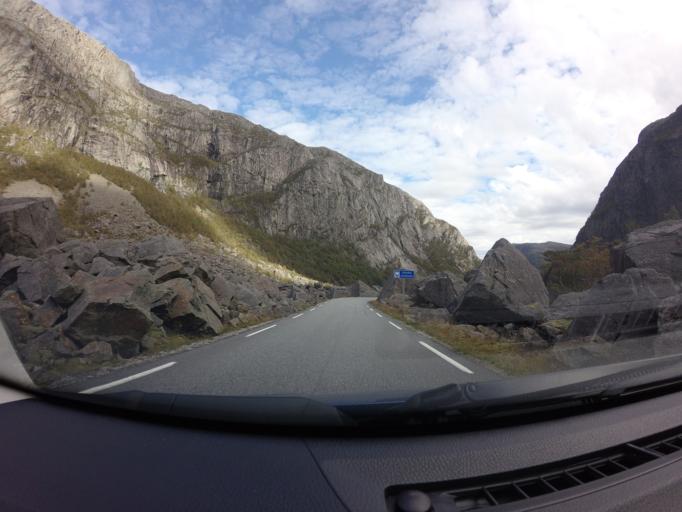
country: NO
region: Rogaland
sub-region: Forsand
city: Forsand
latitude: 58.7682
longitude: 6.2803
